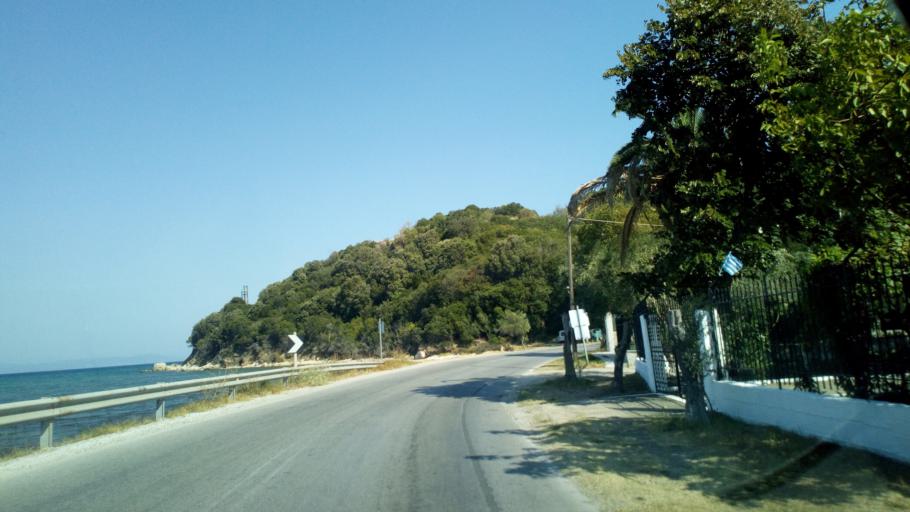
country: GR
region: Central Macedonia
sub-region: Nomos Thessalonikis
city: Stavros
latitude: 40.6580
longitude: 23.7310
